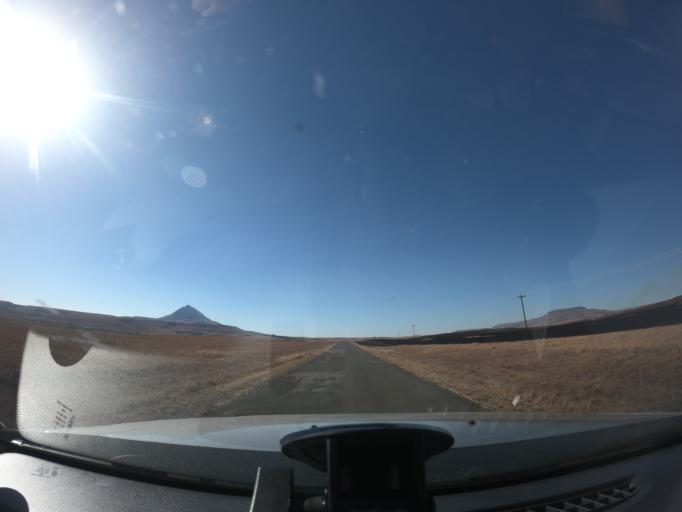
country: ZA
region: KwaZulu-Natal
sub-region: uMgungundlovu District Municipality
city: Impendle
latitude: -29.3876
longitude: 29.7266
